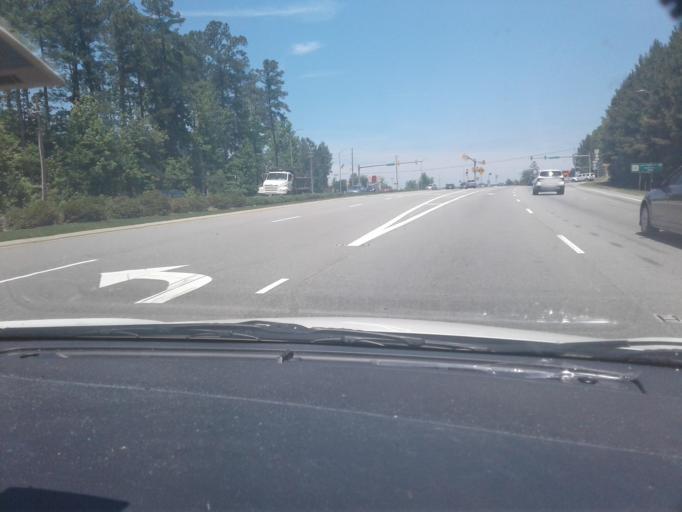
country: US
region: North Carolina
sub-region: Wake County
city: Holly Springs
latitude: 35.6563
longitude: -78.8484
